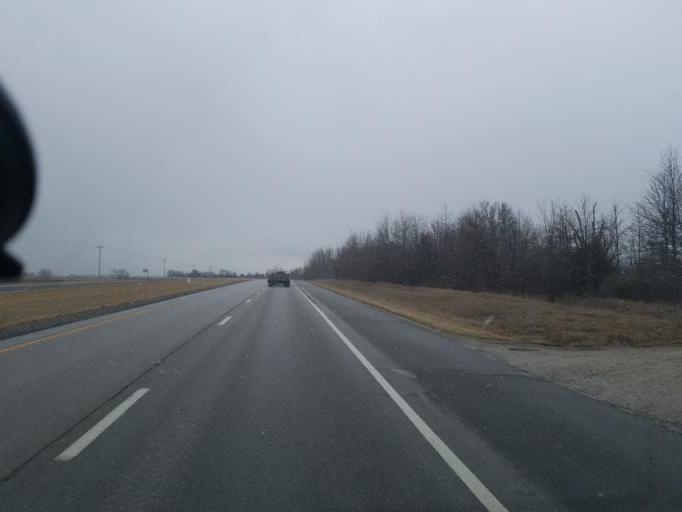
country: US
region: Missouri
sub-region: Macon County
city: Macon
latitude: 39.8719
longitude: -92.4779
